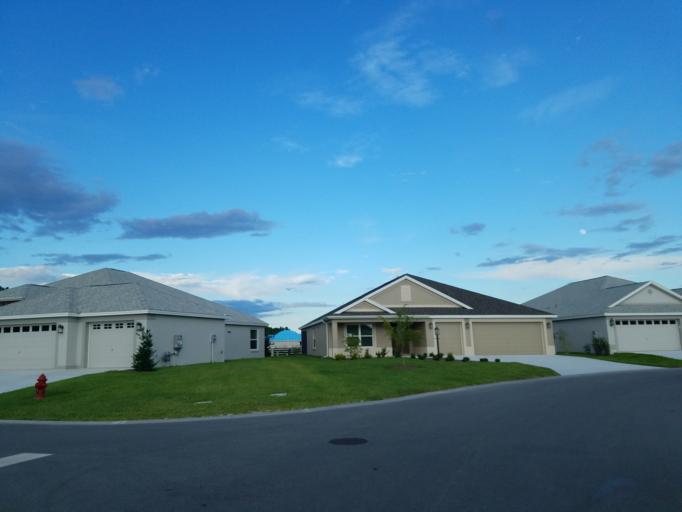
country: US
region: Florida
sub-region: Sumter County
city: Wildwood
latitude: 28.7952
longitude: -82.0217
